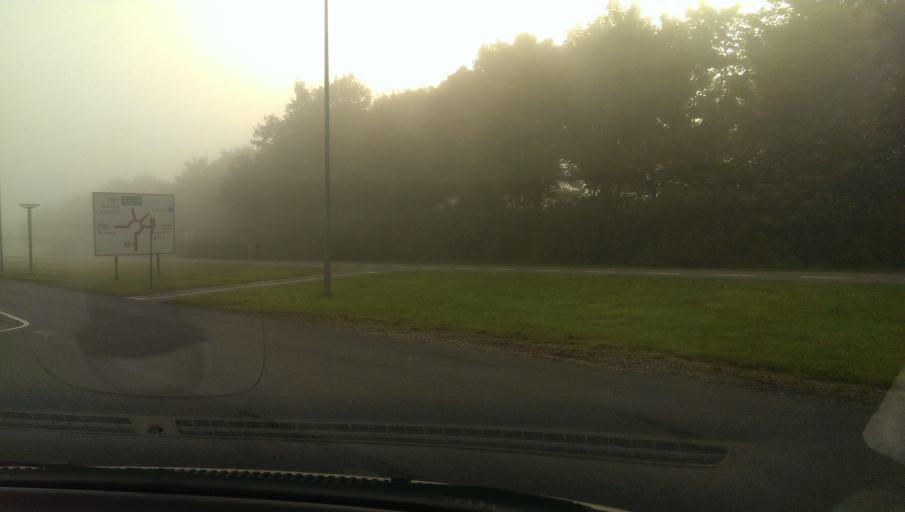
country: DK
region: South Denmark
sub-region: Vejen Kommune
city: Vejen
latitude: 55.4885
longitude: 9.1289
